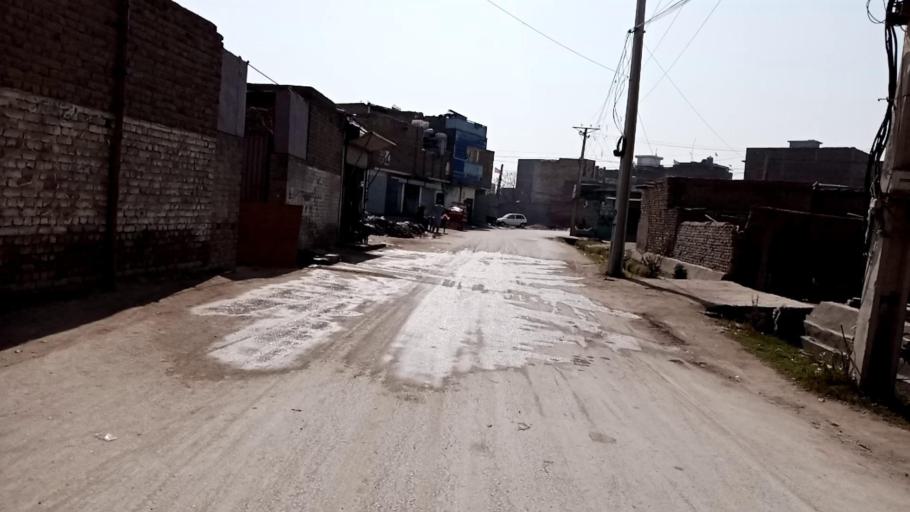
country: PK
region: Khyber Pakhtunkhwa
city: Peshawar
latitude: 34.0125
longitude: 71.5116
